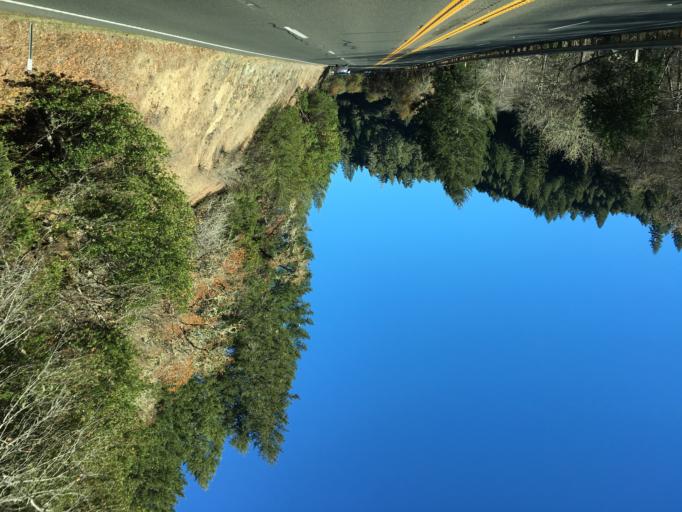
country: US
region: California
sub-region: Mendocino County
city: Brooktrails
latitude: 39.5291
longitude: -123.4034
